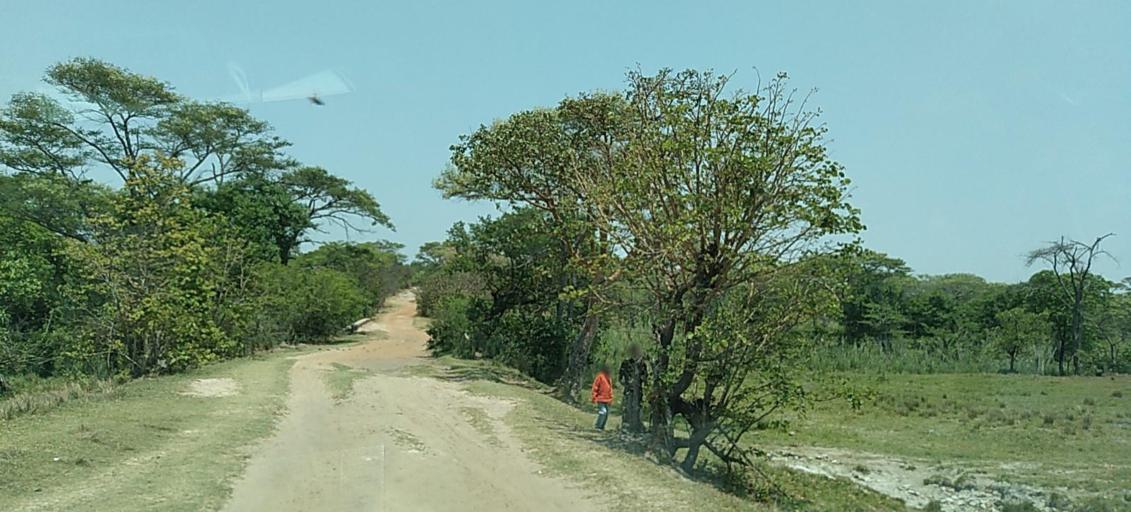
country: ZM
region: Copperbelt
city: Mpongwe
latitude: -13.8671
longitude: 27.8846
